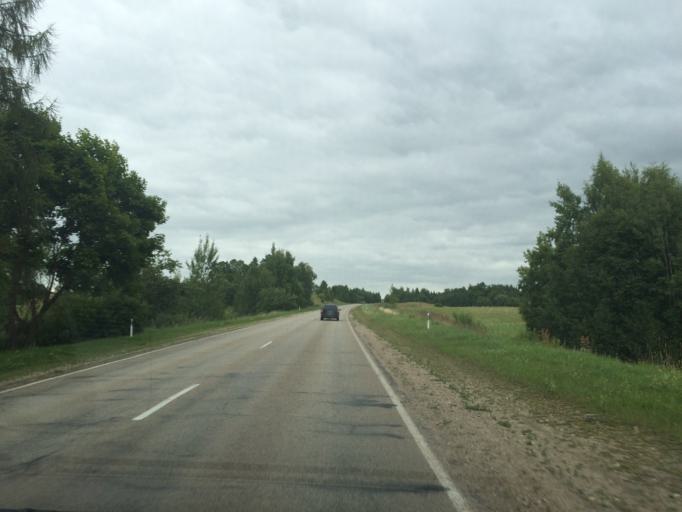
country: LV
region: Rezekne
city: Rezekne
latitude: 56.5774
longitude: 27.3809
